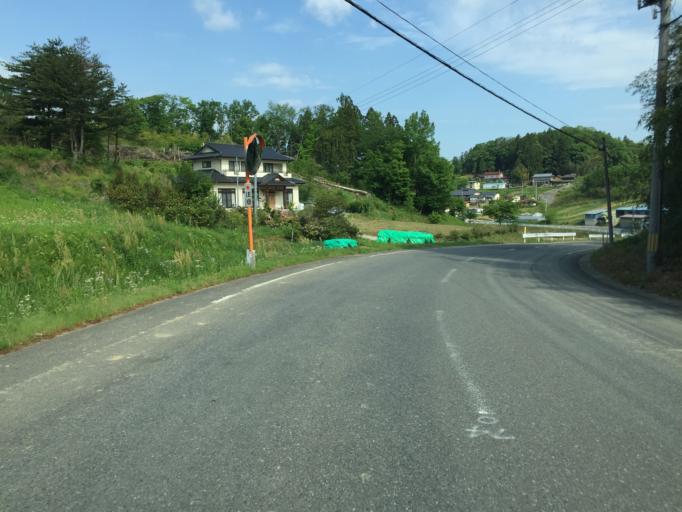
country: JP
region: Fukushima
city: Fukushima-shi
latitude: 37.6654
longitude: 140.4950
